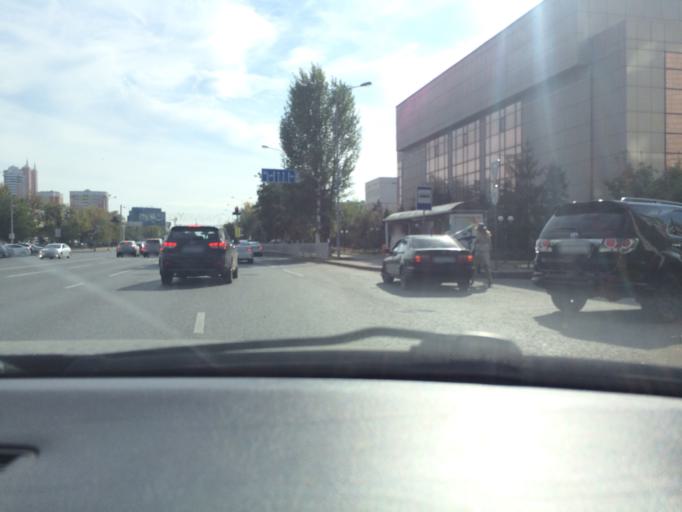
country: KZ
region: Astana Qalasy
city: Astana
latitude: 51.1724
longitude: 71.4253
